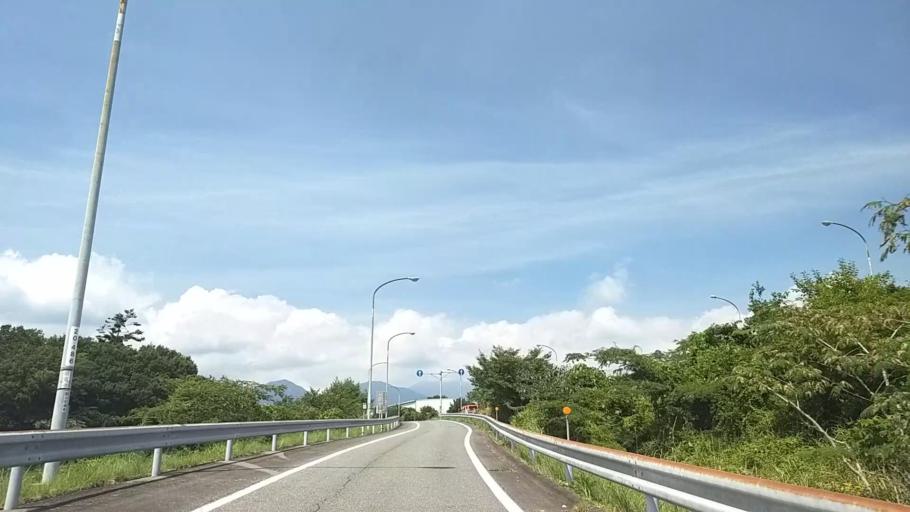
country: JP
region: Shizuoka
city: Fujinomiya
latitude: 35.3121
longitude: 138.6014
